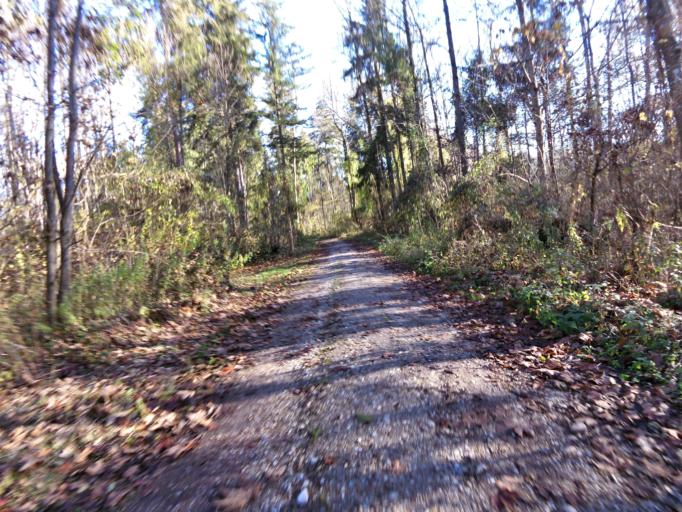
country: DE
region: Bavaria
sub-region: Upper Bavaria
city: Wang
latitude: 48.5061
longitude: 11.9741
